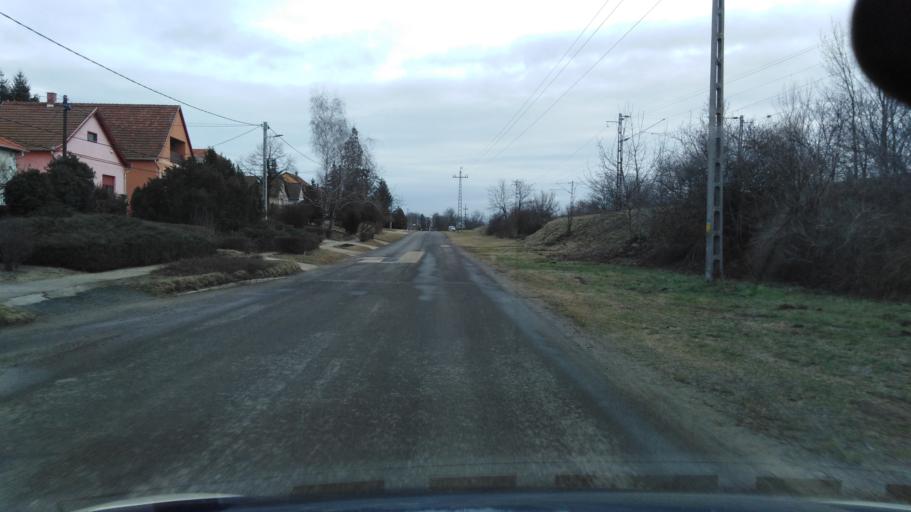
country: HU
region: Heves
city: Hatvan
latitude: 47.6747
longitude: 19.6963
